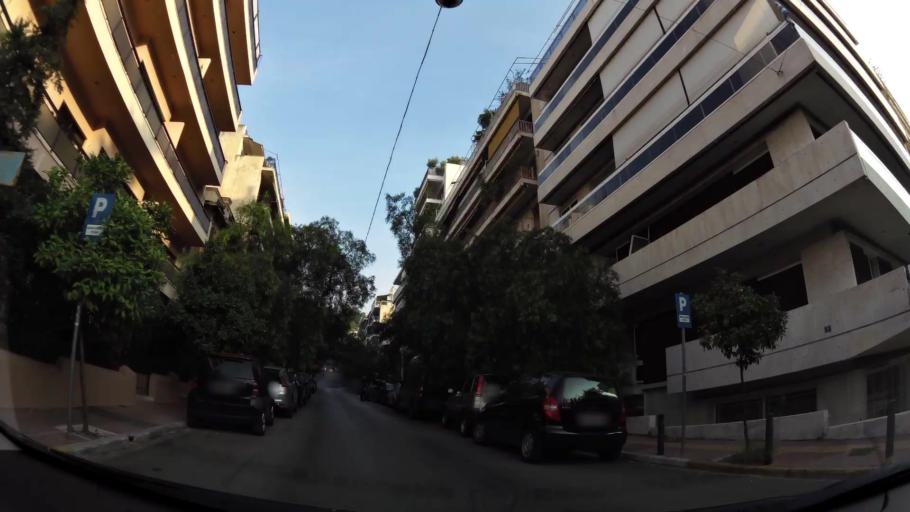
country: GR
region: Attica
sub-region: Nomarchia Athinas
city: Vyronas
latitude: 37.9792
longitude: 23.7494
